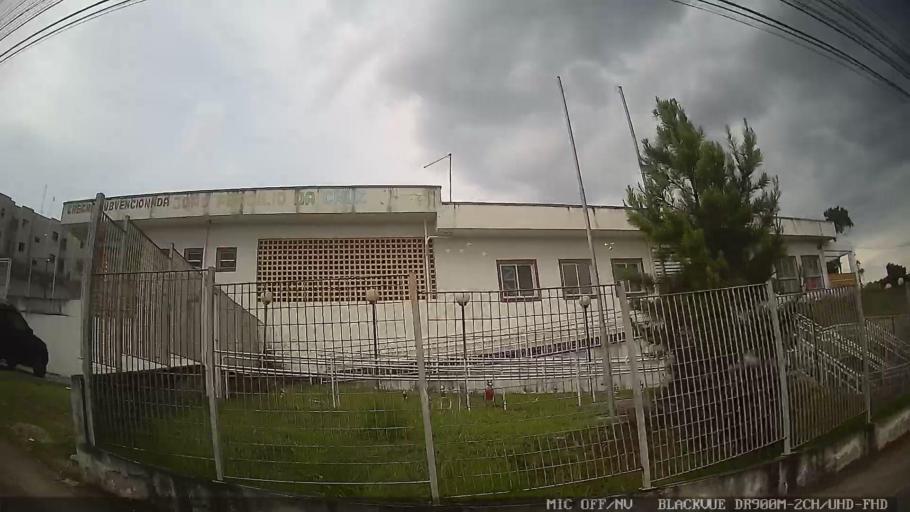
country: BR
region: Sao Paulo
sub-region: Itaquaquecetuba
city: Itaquaquecetuba
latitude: -23.4700
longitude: -46.3139
